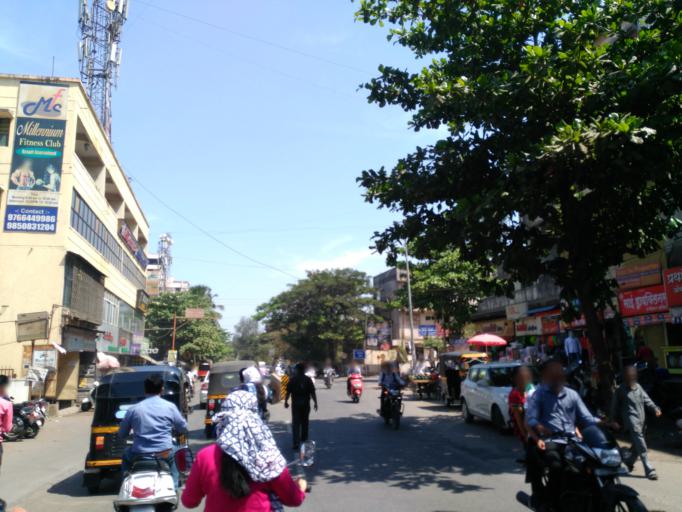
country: IN
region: Maharashtra
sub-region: Pune Division
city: Pune
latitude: 18.4536
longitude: 73.8511
